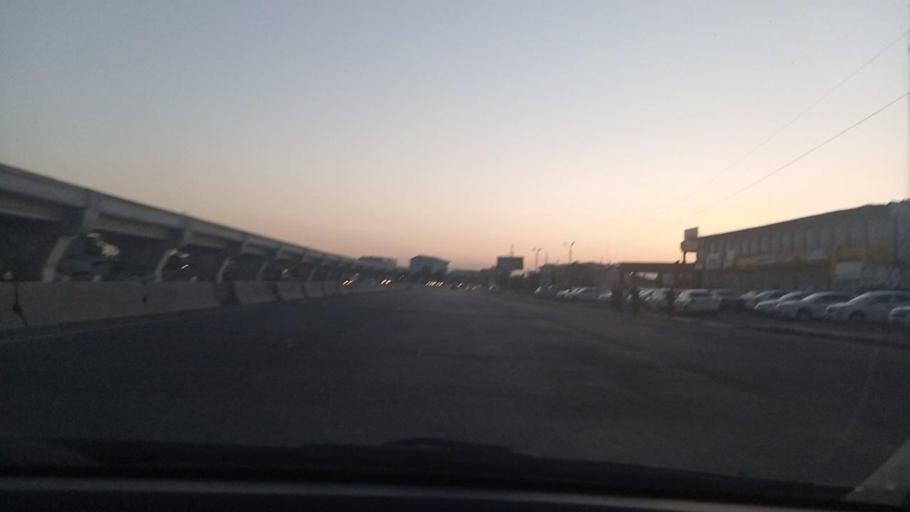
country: UZ
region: Toshkent Shahri
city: Bektemir
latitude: 41.2408
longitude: 69.3353
